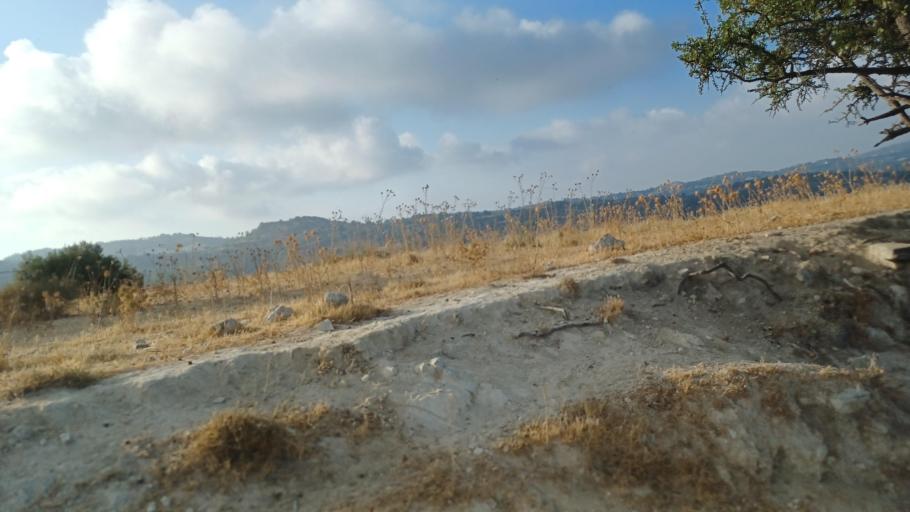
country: CY
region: Pafos
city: Mesogi
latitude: 34.8476
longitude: 32.5798
